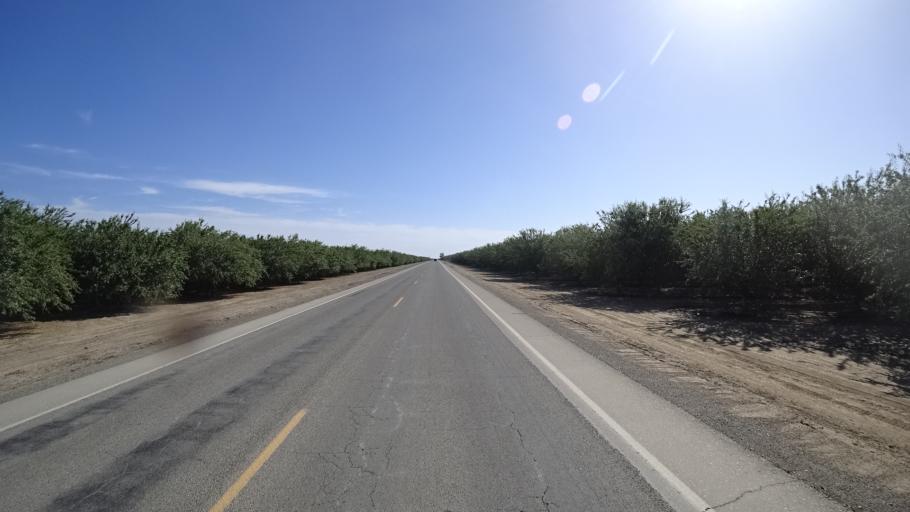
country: US
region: California
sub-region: Fresno County
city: Huron
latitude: 36.1314
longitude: -120.0195
